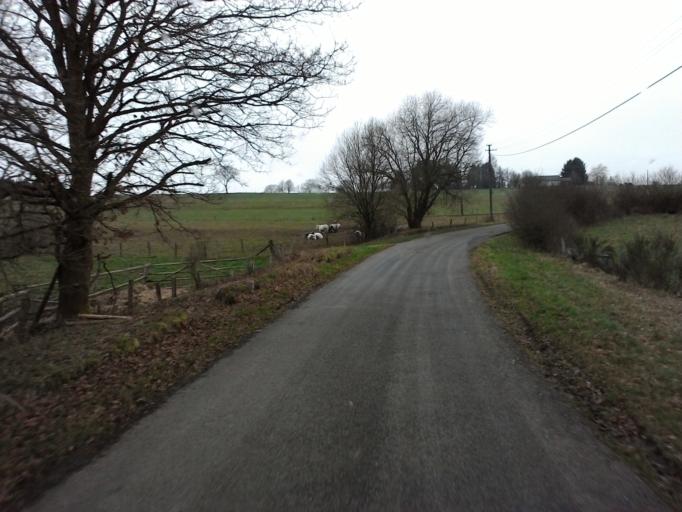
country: BE
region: Wallonia
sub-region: Province de Namur
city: Gedinne
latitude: 50.0212
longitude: 4.8634
